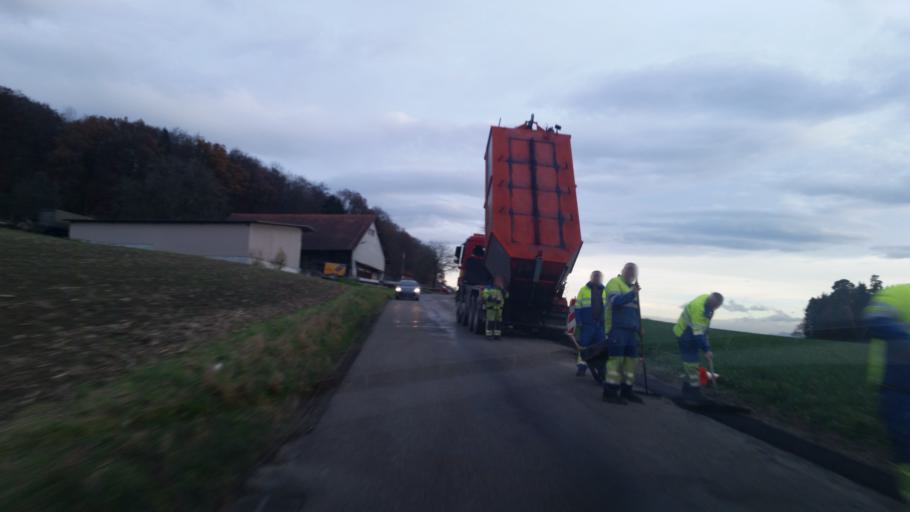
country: CH
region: Aargau
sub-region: Bezirk Baden
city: Kunten
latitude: 47.3832
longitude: 8.3415
